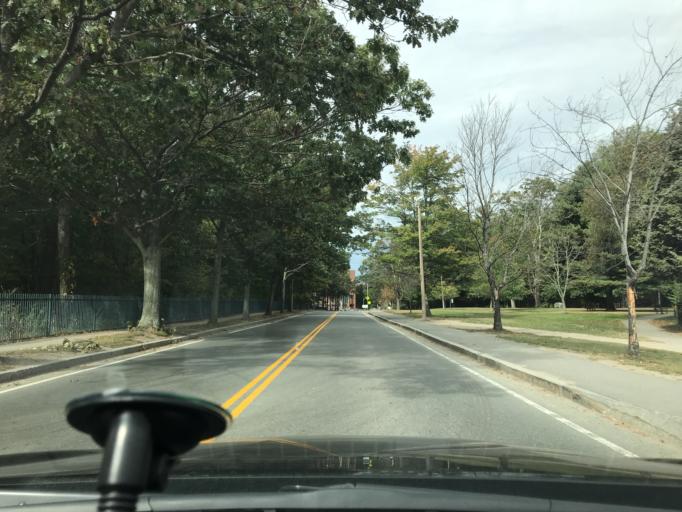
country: US
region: Massachusetts
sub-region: Middlesex County
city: Watertown
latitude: 42.3351
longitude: -71.1628
